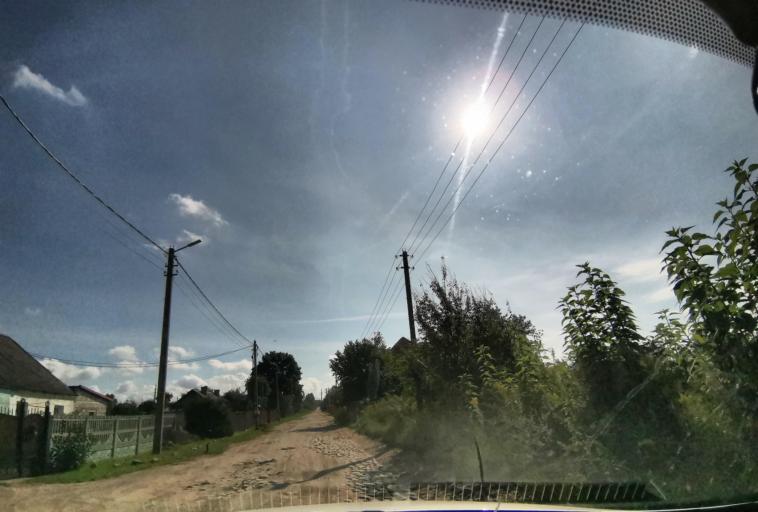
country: RU
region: Kaliningrad
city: Chernyakhovsk
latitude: 54.6605
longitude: 21.8387
